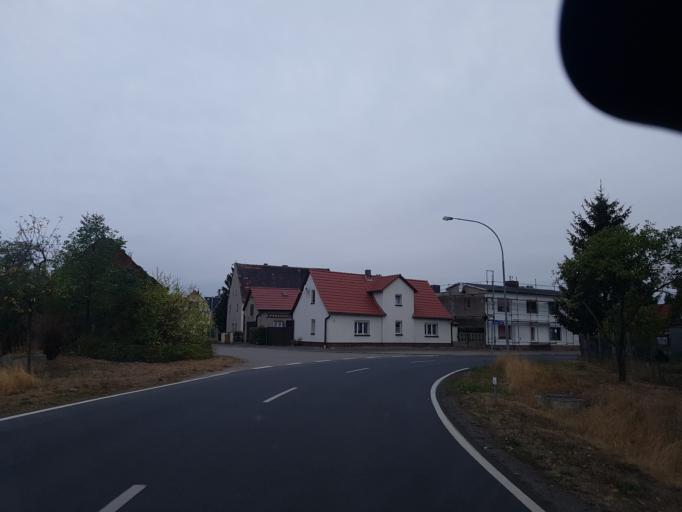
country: DE
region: Saxony
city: Arzberg
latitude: 51.5201
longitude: 13.1413
